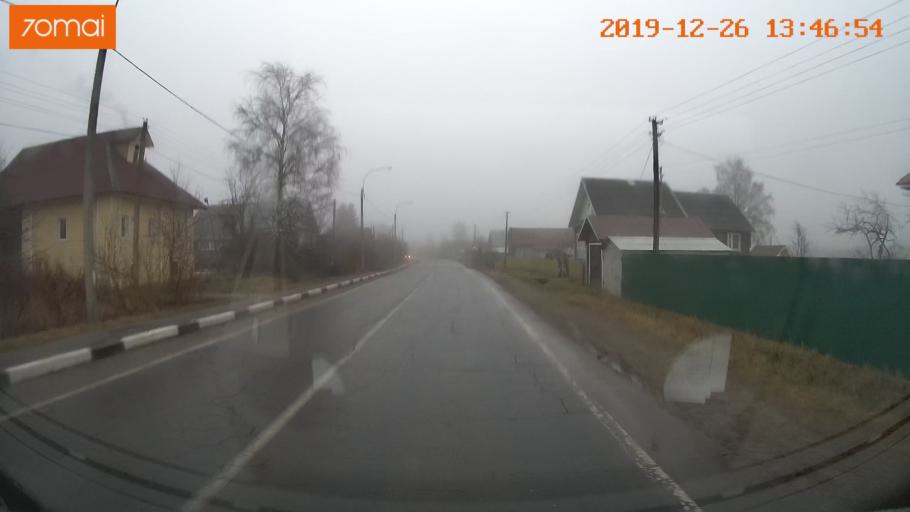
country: RU
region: Vologda
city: Sheksna
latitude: 58.6884
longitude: 38.5298
